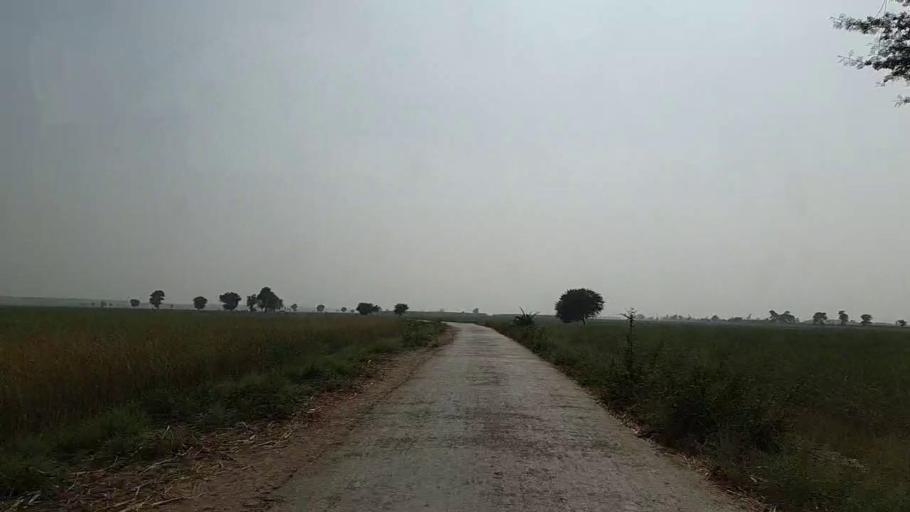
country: PK
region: Sindh
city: Naukot
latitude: 24.7649
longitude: 69.3481
